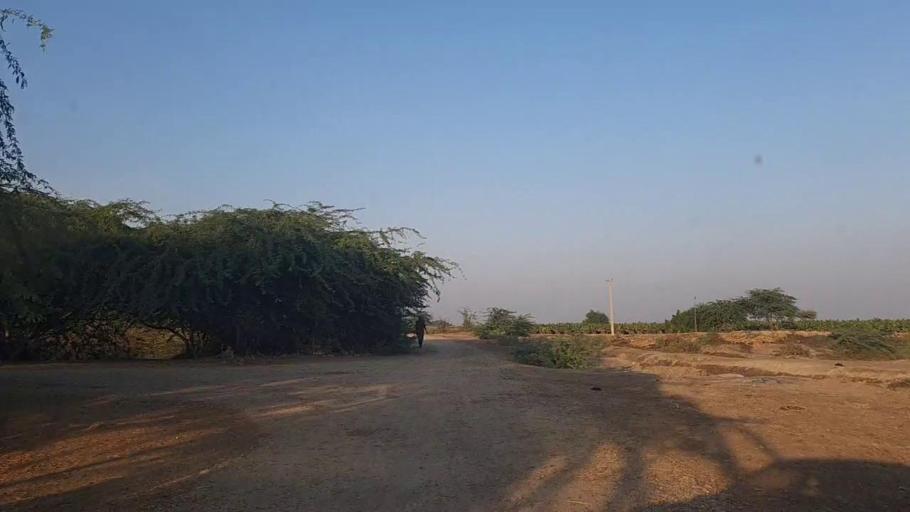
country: PK
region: Sindh
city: Thatta
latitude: 24.6799
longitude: 67.9489
